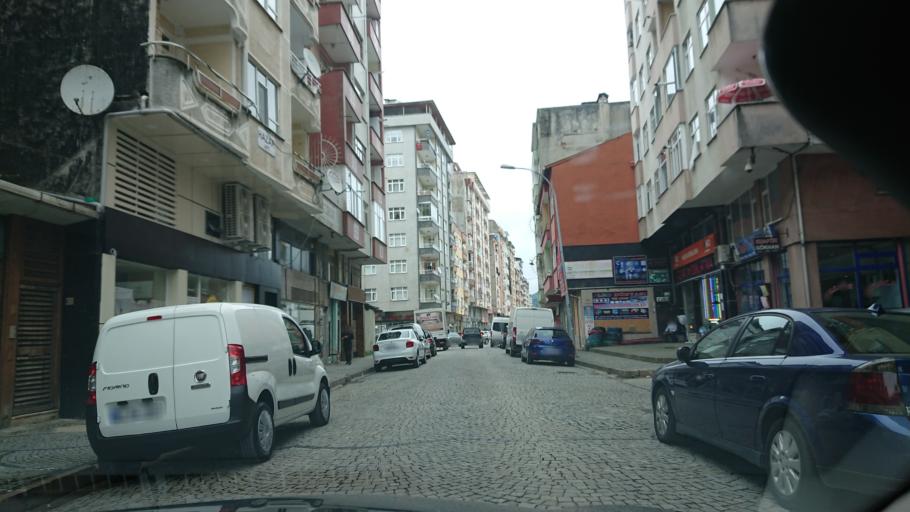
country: TR
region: Rize
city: Rize
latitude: 41.0240
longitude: 40.5310
